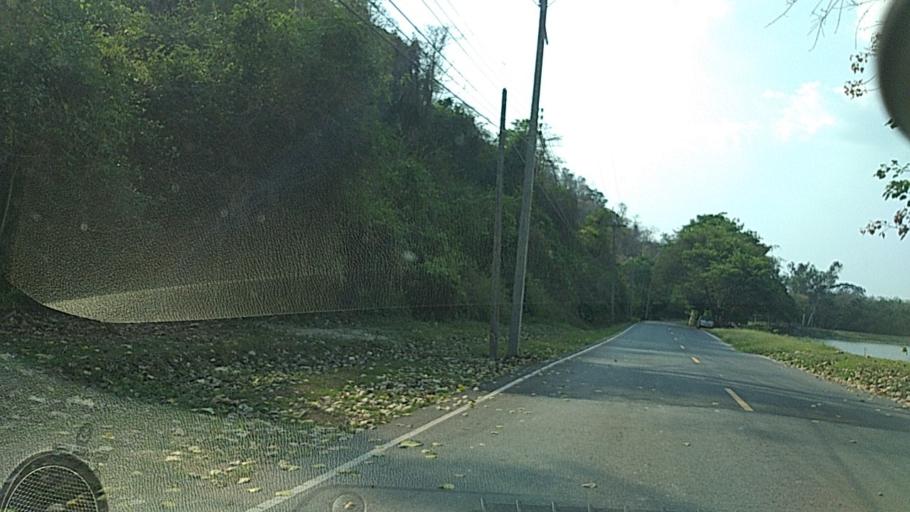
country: TH
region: Sara Buri
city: Wihan Daeng
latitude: 14.4415
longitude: 100.9593
